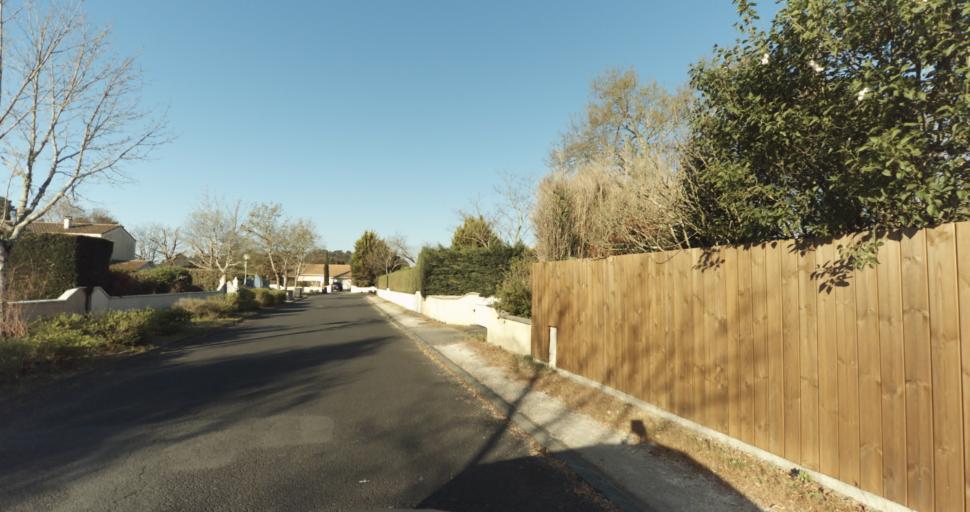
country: FR
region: Aquitaine
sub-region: Departement de la Gironde
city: Martignas-sur-Jalle
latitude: 44.8098
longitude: -0.7971
